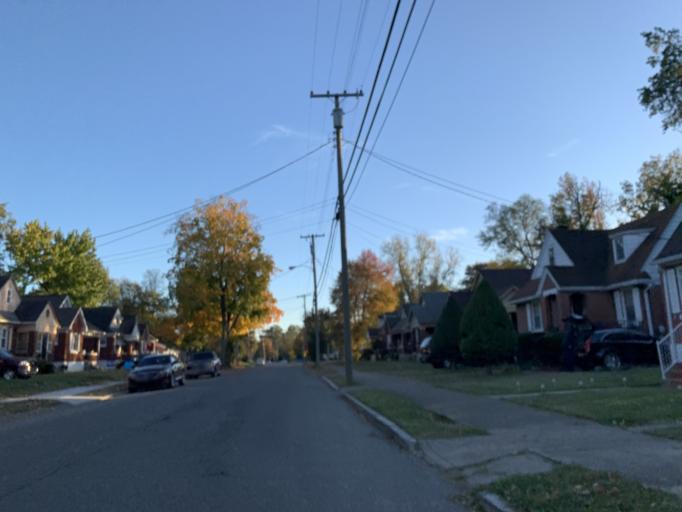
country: US
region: Indiana
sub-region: Floyd County
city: New Albany
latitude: 38.2484
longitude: -85.8273
